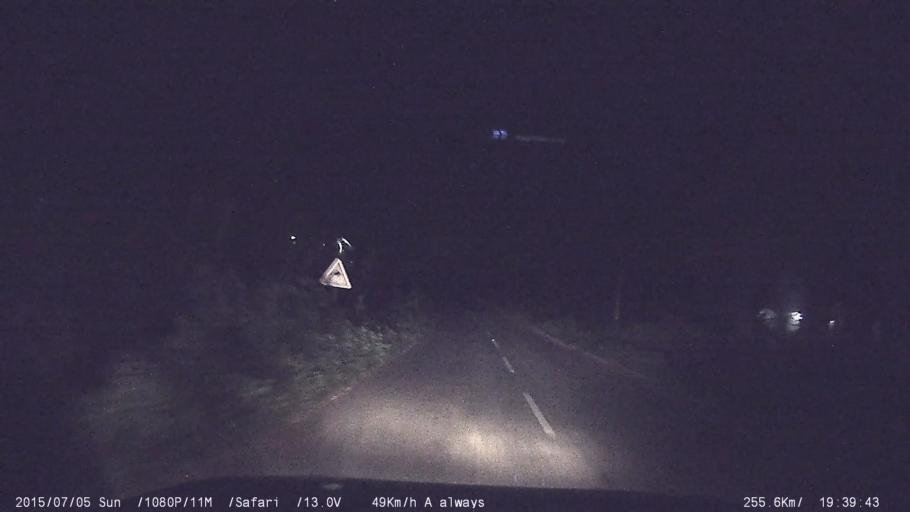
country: IN
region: Kerala
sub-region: Palakkad district
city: Palakkad
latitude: 10.7482
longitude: 76.5625
